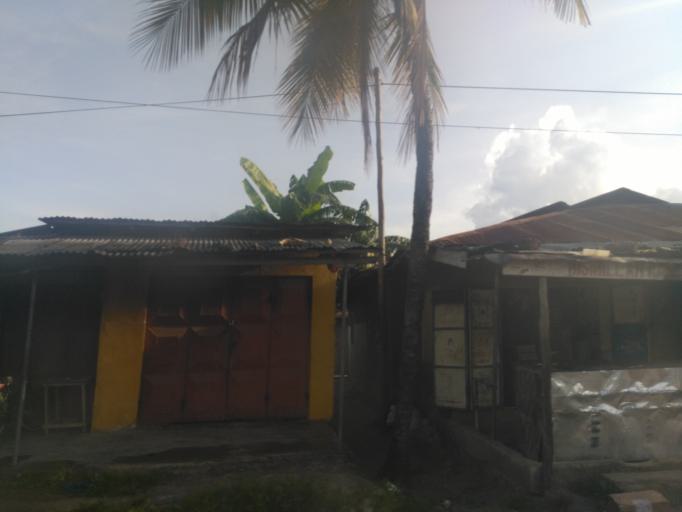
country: TZ
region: Zanzibar Urban/West
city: Zanzibar
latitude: -6.1776
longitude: 39.2145
